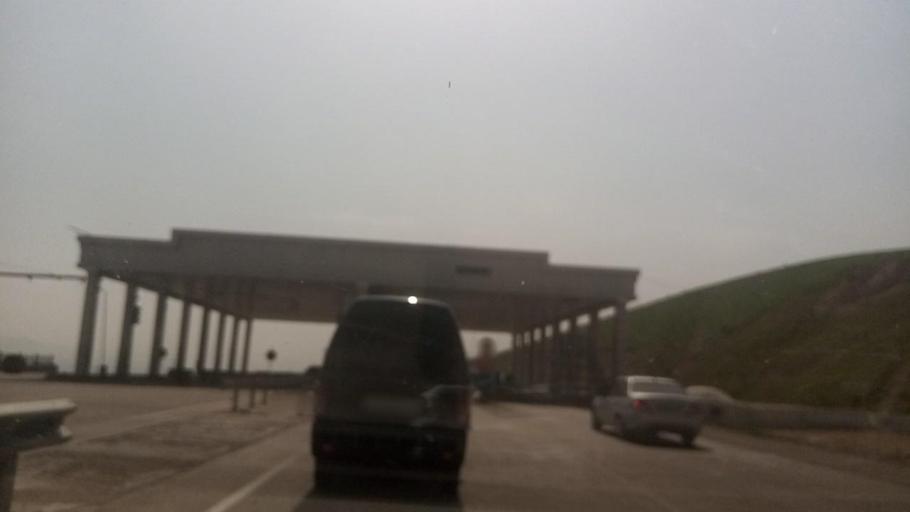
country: UZ
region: Toshkent
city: Angren
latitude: 41.0645
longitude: 70.2156
